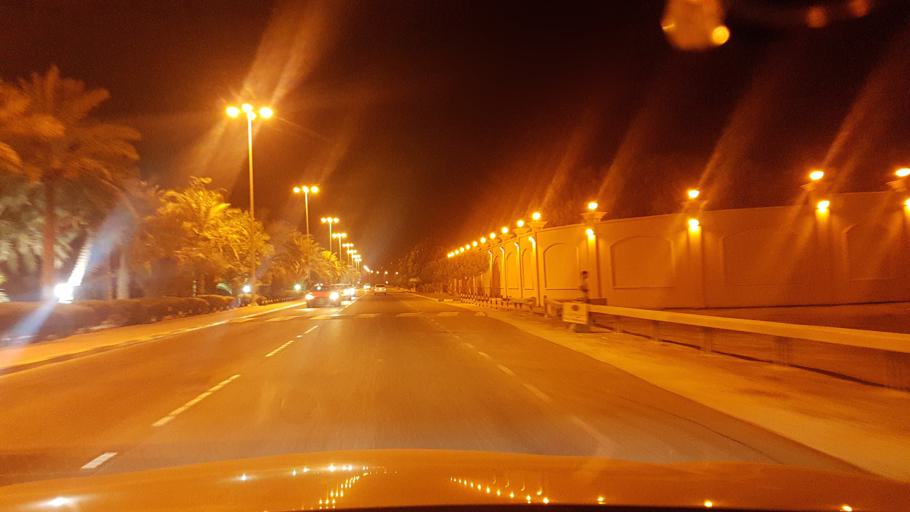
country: BH
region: Central Governorate
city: Dar Kulayb
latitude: 26.0458
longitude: 50.4884
